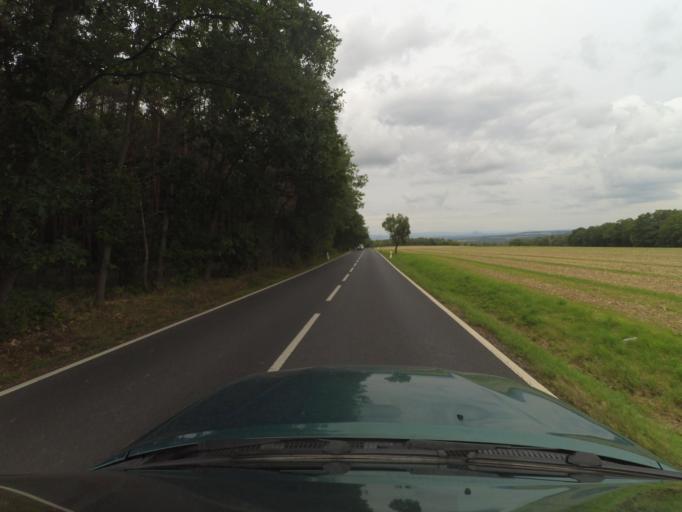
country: CZ
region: Ustecky
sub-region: Okres Louny
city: Louny
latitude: 50.2773
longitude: 13.7738
